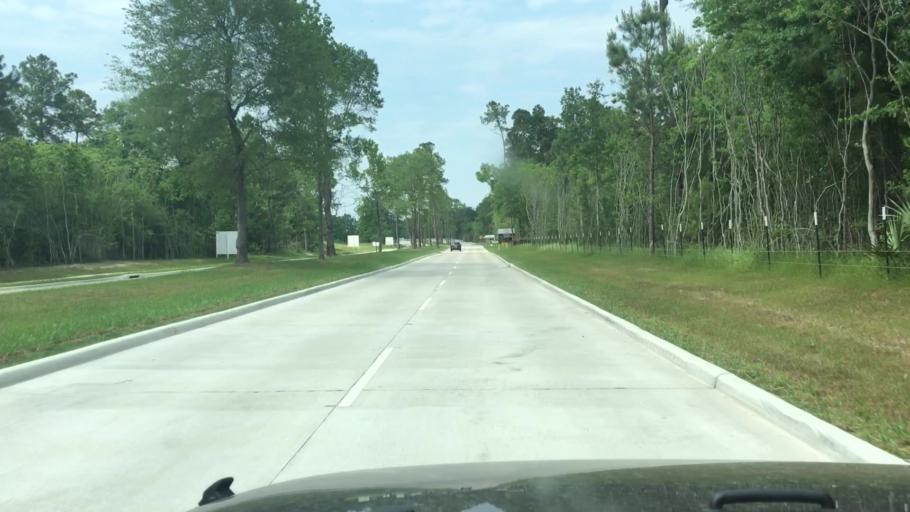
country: US
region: Texas
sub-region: Harris County
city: Atascocita
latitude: 29.9565
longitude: -95.2100
